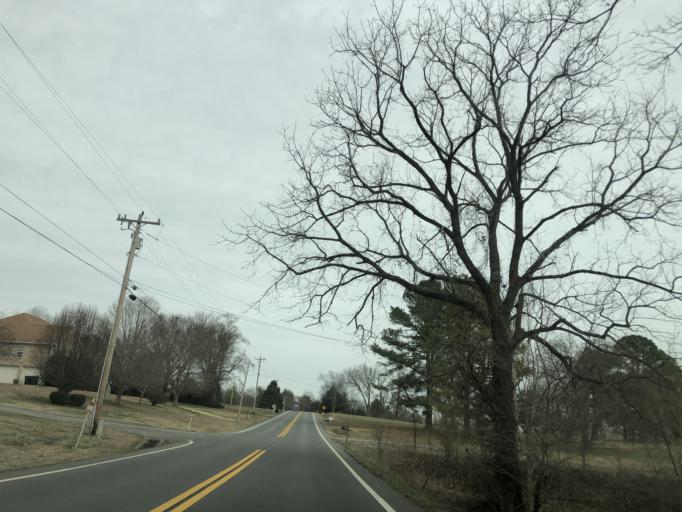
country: US
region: Tennessee
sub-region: Robertson County
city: Greenbrier
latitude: 36.4808
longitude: -86.7852
